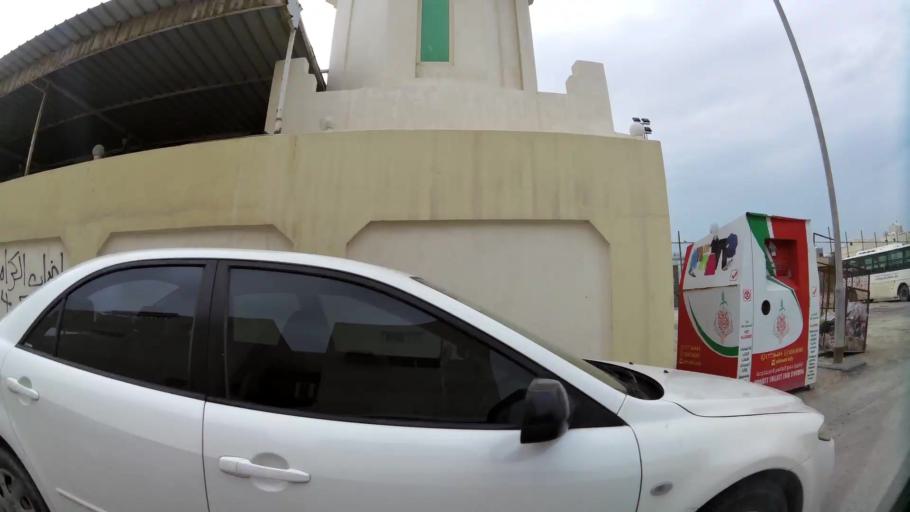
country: BH
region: Northern
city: Sitrah
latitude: 26.1673
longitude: 50.6098
